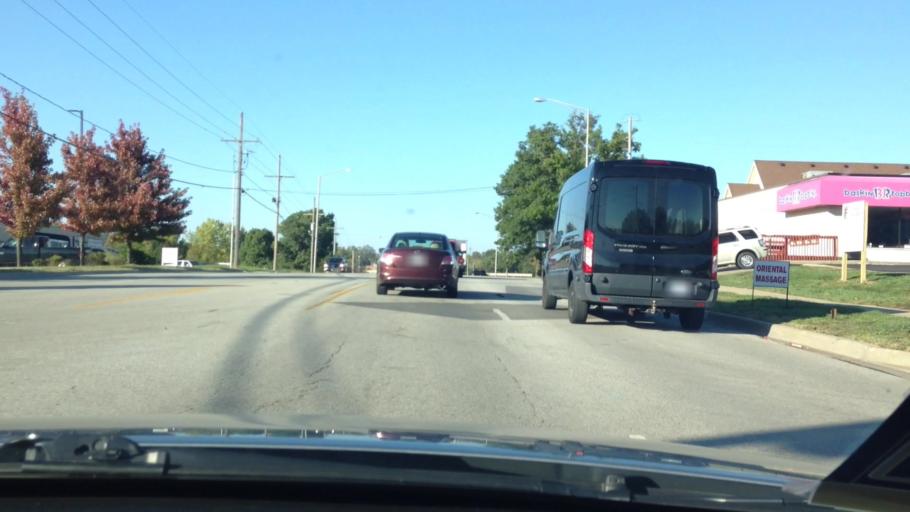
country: US
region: Missouri
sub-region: Clay County
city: Gladstone
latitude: 39.2339
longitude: -94.5761
